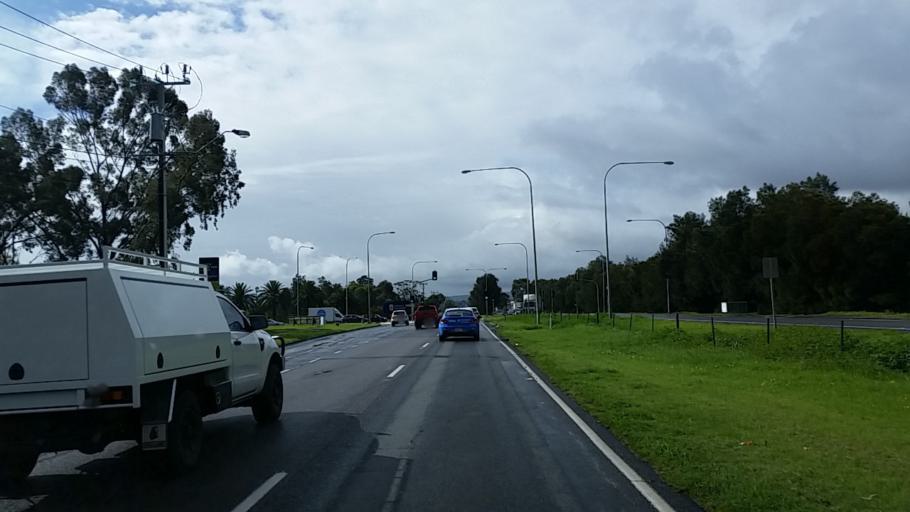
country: AU
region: South Australia
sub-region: Salisbury
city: Ingle Farm
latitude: -34.8171
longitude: 138.6243
